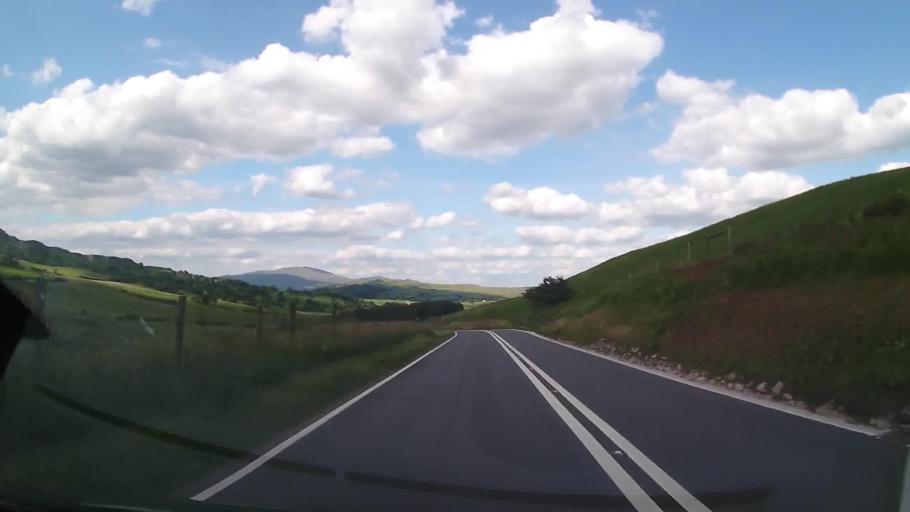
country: GB
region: Wales
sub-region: Gwynedd
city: Dolgellau
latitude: 52.7134
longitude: -3.8399
